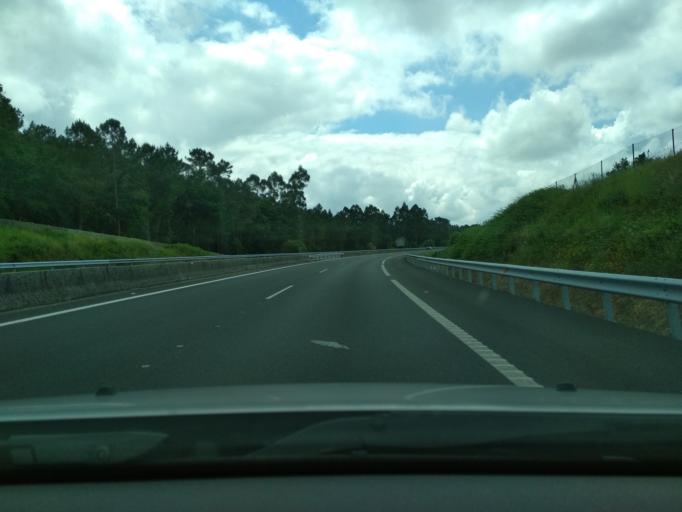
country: ES
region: Galicia
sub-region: Provincia de Pontevedra
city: Portas
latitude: 42.5528
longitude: -8.6682
